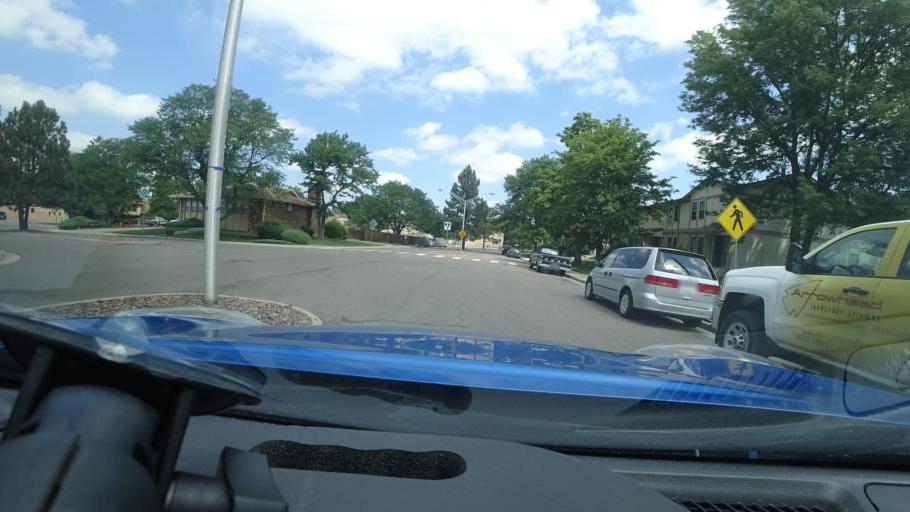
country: US
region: Colorado
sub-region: Adams County
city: Aurora
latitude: 39.7194
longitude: -104.8488
